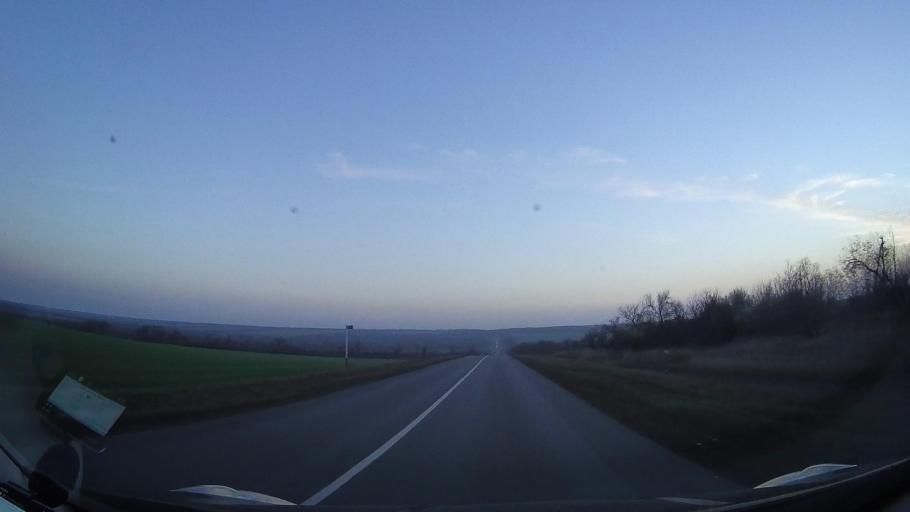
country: RU
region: Rostov
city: Zernograd
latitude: 46.9071
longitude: 40.3389
